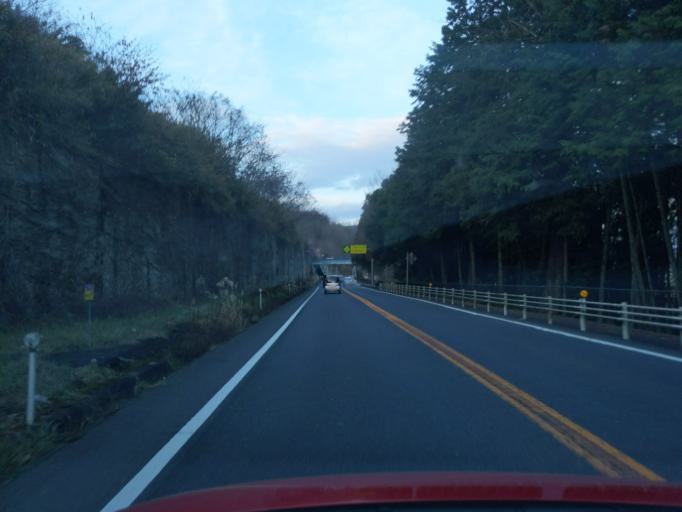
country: JP
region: Gifu
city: Mizunami
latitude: 35.4259
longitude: 137.3288
